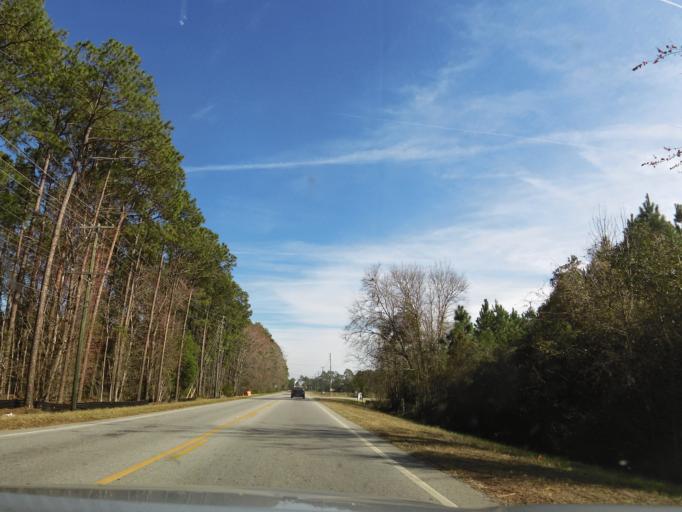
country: US
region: Georgia
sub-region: Glynn County
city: Dock Junction
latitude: 31.2725
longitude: -81.5456
